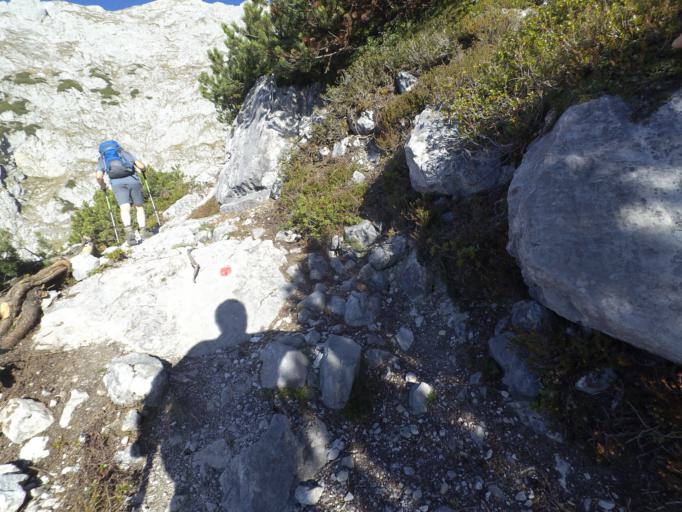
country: AT
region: Salzburg
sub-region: Politischer Bezirk Sankt Johann im Pongau
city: Werfenweng
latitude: 47.4930
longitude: 13.2324
